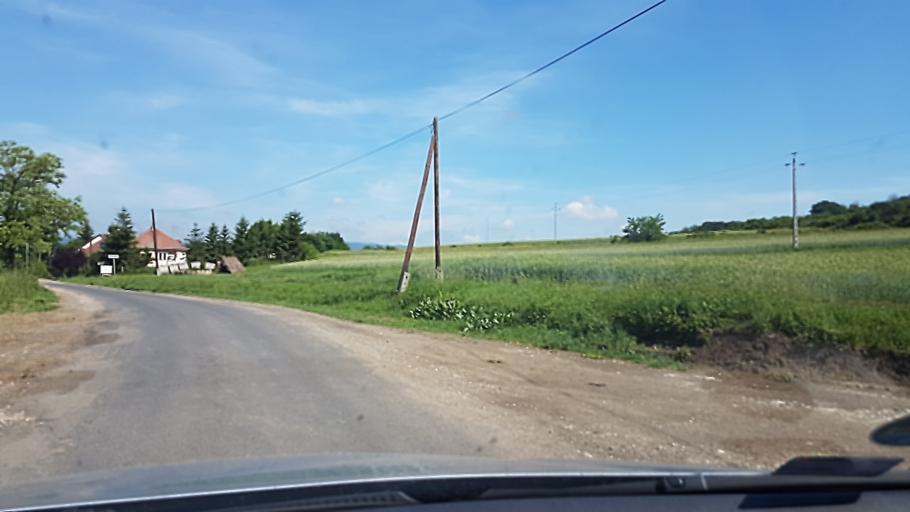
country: HU
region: Borsod-Abauj-Zemplen
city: Saly
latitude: 47.9506
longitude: 20.6996
